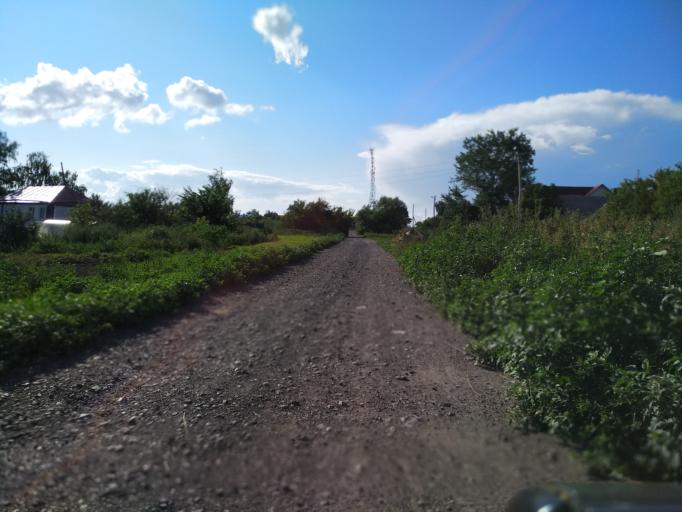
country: RU
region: Lipetsk
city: Dobrinka
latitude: 52.0335
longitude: 40.5619
